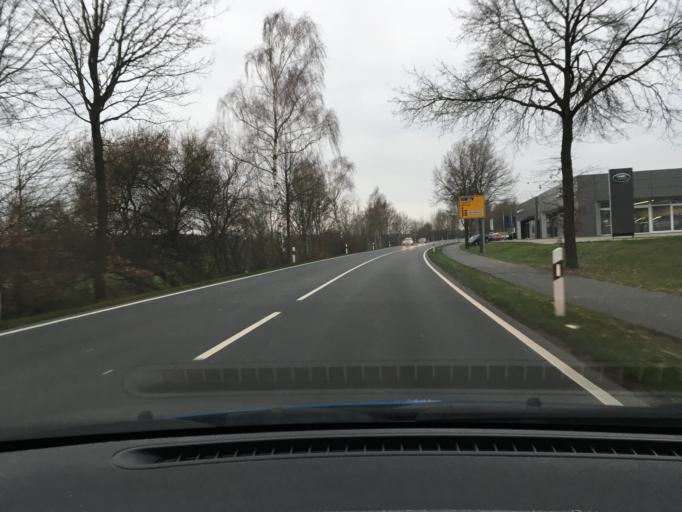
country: DE
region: Lower Saxony
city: Walsrode
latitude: 52.8659
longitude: 9.6252
